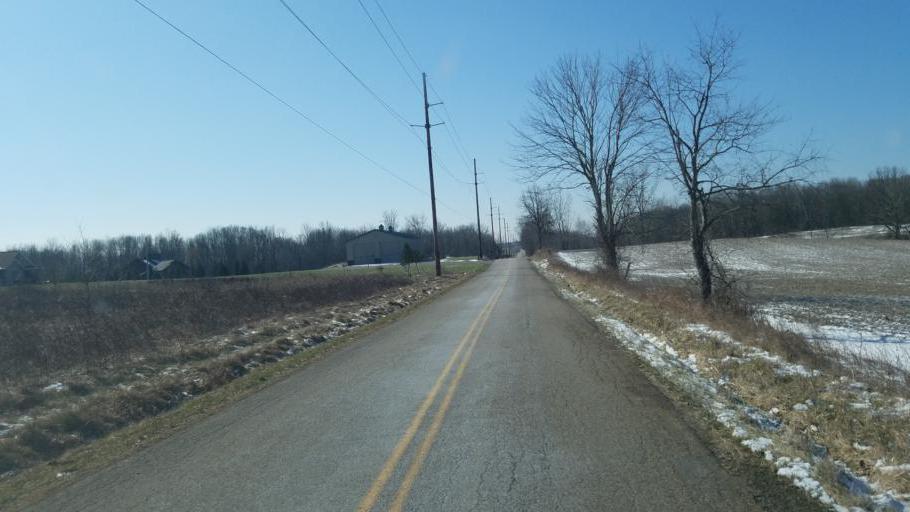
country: US
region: Ohio
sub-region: Knox County
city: Mount Vernon
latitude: 40.3132
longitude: -82.4727
